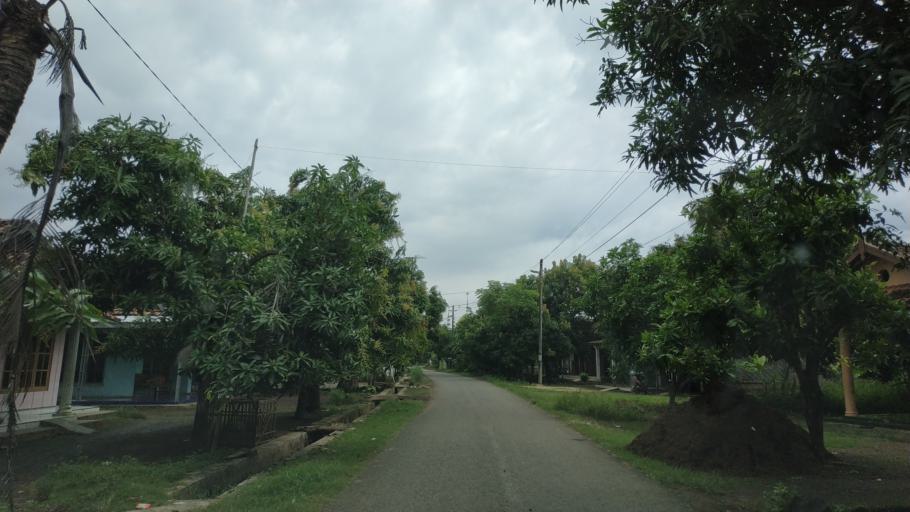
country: ID
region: Central Java
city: Krajan Tegalombo
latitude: -6.4228
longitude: 110.9825
